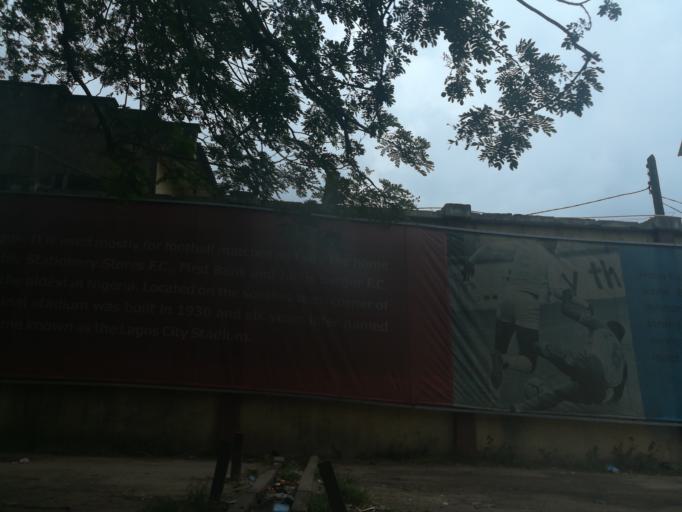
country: NG
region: Lagos
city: Lagos
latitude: 6.4425
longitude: 3.4012
